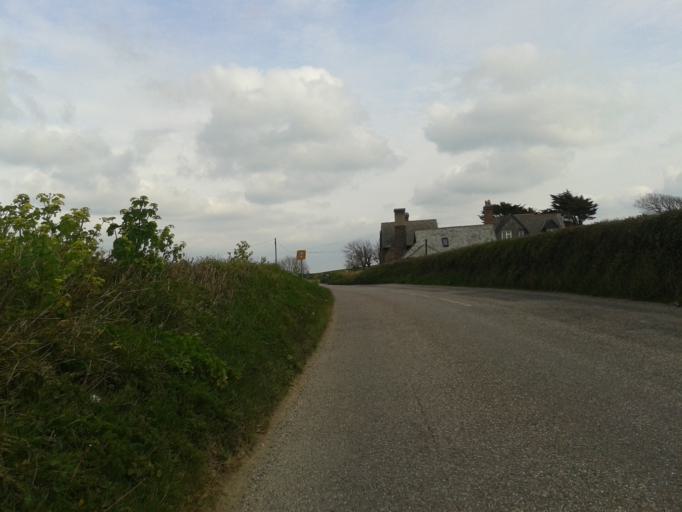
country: GB
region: England
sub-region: Devon
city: Braunton
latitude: 51.1797
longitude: -4.1831
